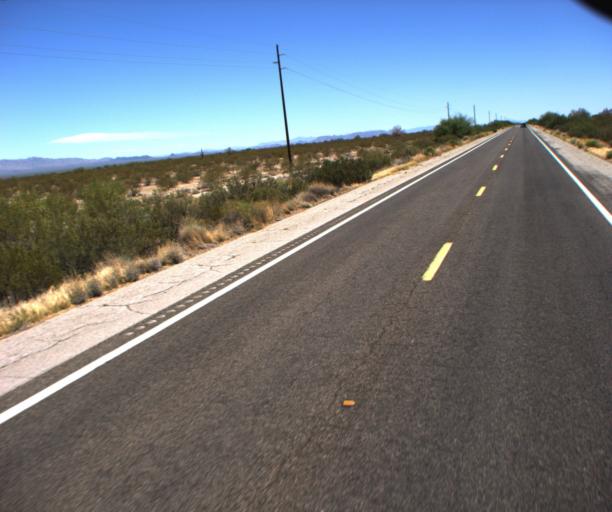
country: US
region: Arizona
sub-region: La Paz County
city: Salome
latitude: 33.8609
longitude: -113.4200
